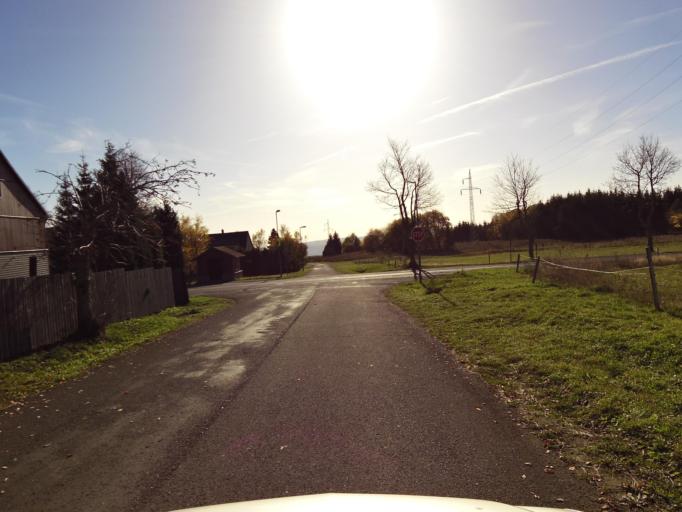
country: CZ
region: Ustecky
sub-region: Okres Chomutov
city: Perstejn
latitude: 50.4216
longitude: 13.1117
